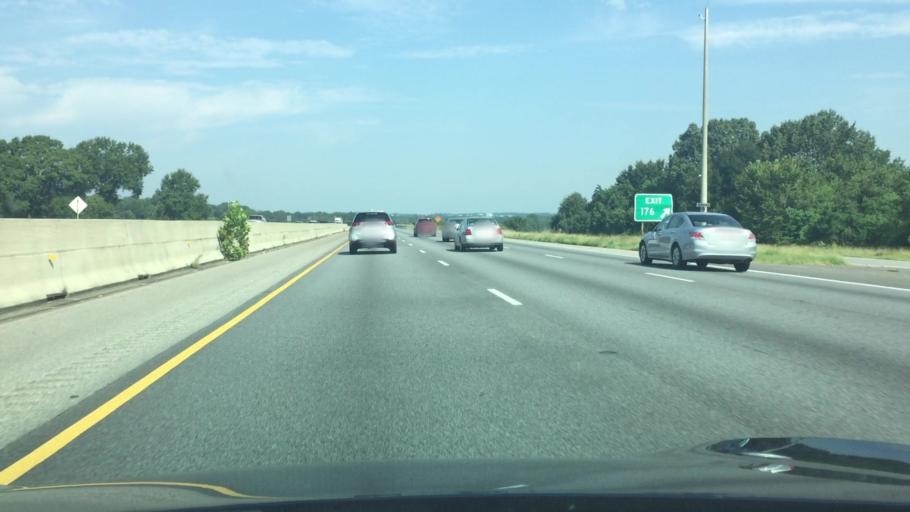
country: US
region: Alabama
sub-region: Elmore County
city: Millbrook
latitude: 32.4152
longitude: -86.3537
